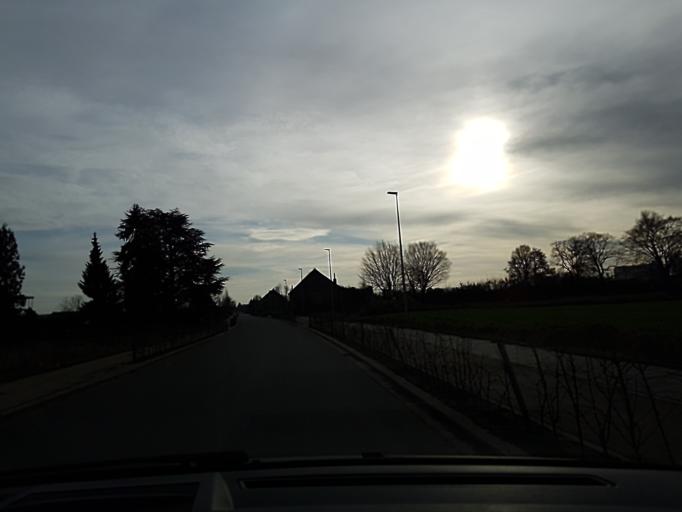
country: BE
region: Flanders
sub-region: Provincie Vlaams-Brabant
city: Herent
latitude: 50.9403
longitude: 4.6833
